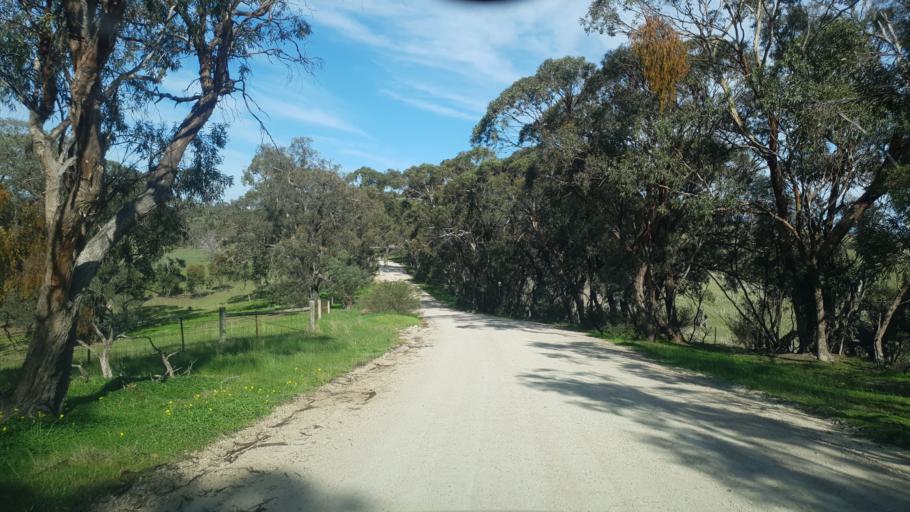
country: AU
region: South Australia
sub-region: Playford
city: One Tree Hill
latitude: -34.6451
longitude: 138.8130
